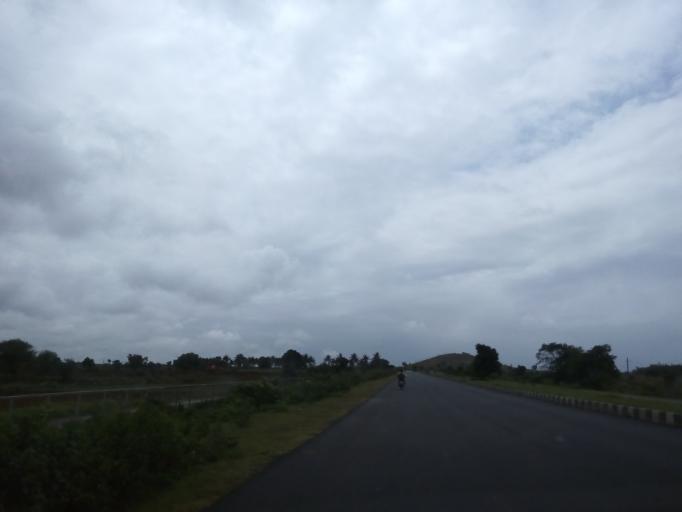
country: IN
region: Karnataka
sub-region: Haveri
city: Byadgi
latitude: 14.7162
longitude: 75.4950
